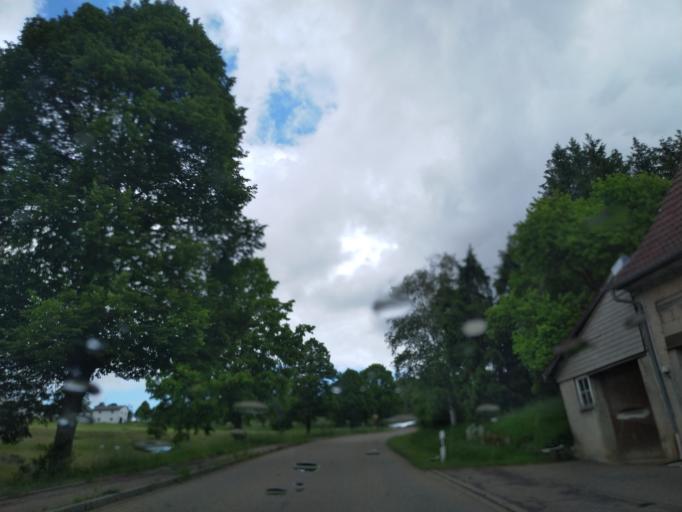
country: DE
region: Baden-Wuerttemberg
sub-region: Freiburg Region
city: Loffingen
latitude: 47.8596
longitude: 8.3130
